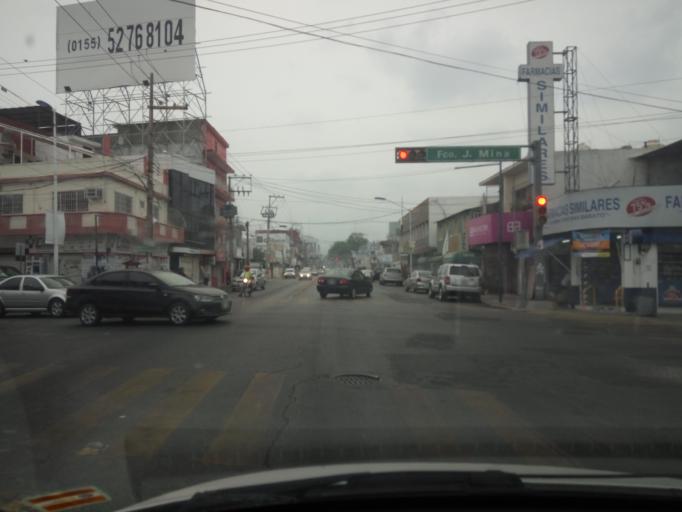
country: MX
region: Tabasco
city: Villahermosa
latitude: 17.9942
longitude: -92.9220
